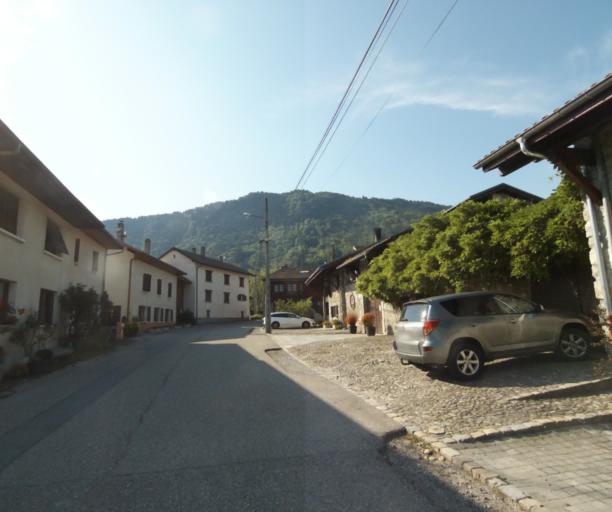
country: FR
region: Rhone-Alpes
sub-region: Departement de la Haute-Savoie
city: Allinges
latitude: 46.3112
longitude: 6.4792
